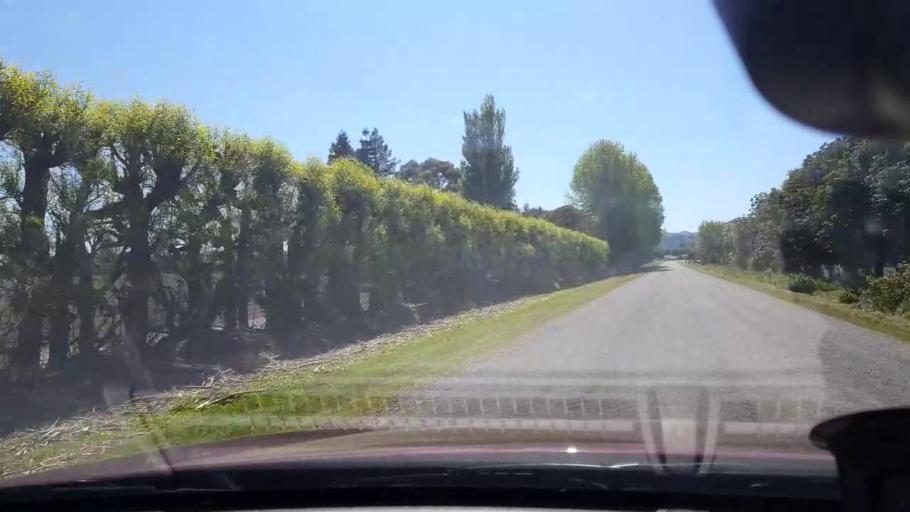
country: NZ
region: Gisborne
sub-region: Gisborne District
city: Gisborne
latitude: -38.6394
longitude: 177.9384
